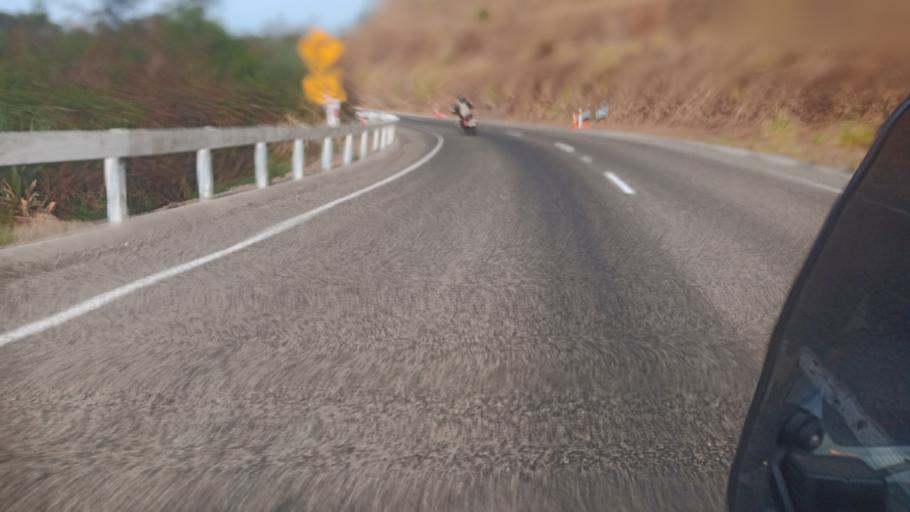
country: NZ
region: Bay of Plenty
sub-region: Opotiki District
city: Opotiki
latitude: -37.8894
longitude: 177.5563
